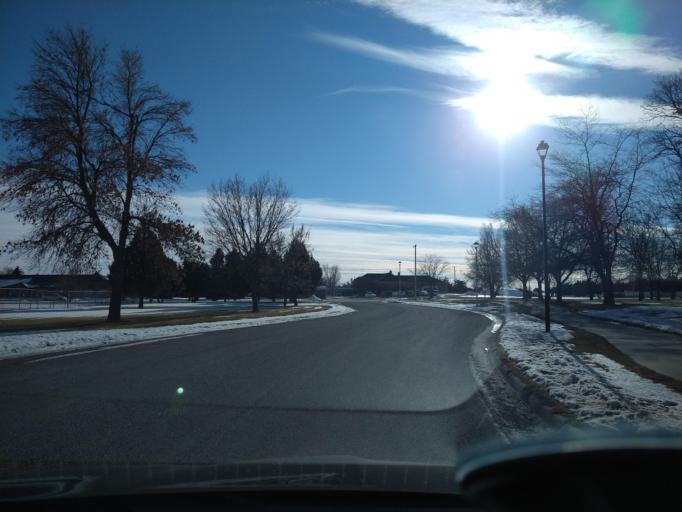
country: US
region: Nebraska
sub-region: Sheridan County
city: Rushville
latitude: 42.7175
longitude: -102.4668
